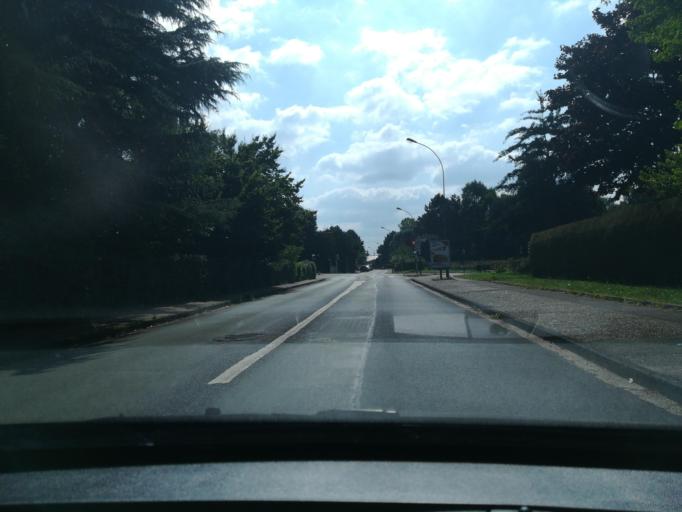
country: FR
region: Haute-Normandie
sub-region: Departement de la Seine-Maritime
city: Bois-Guillaume
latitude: 49.4627
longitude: 1.1094
